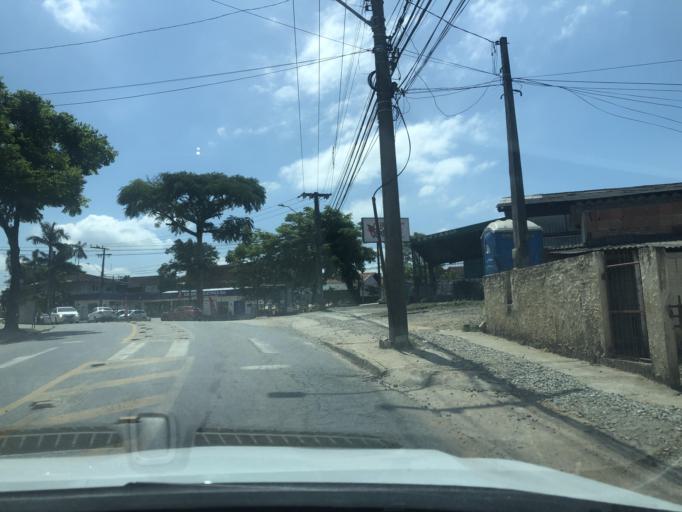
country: BR
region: Santa Catarina
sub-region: Joinville
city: Joinville
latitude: -26.3310
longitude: -48.8265
